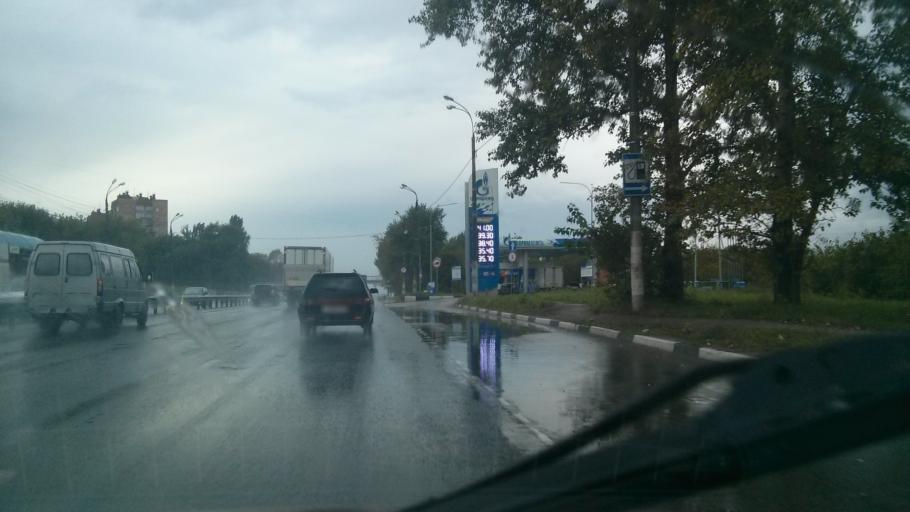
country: RU
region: Nizjnij Novgorod
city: Nizhniy Novgorod
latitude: 56.2425
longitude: 43.9749
